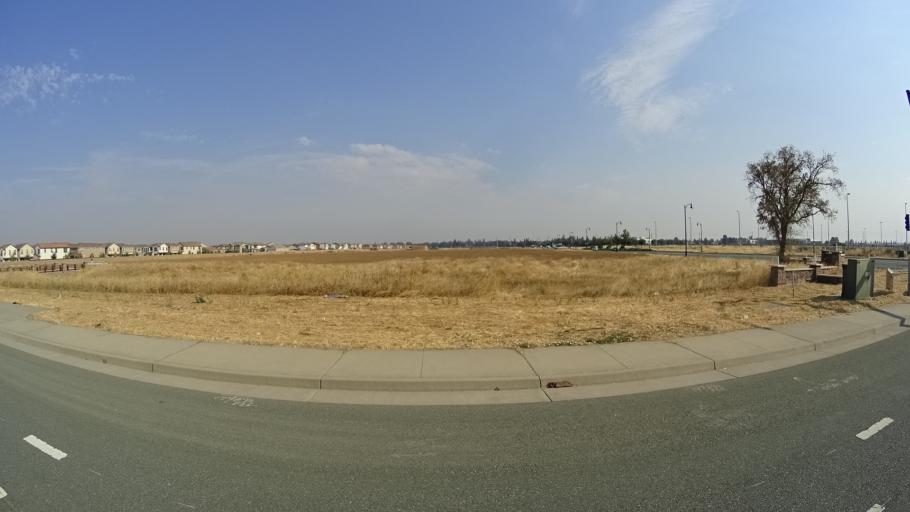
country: US
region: California
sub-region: Sacramento County
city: Elk Grove
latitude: 38.3790
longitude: -121.3733
